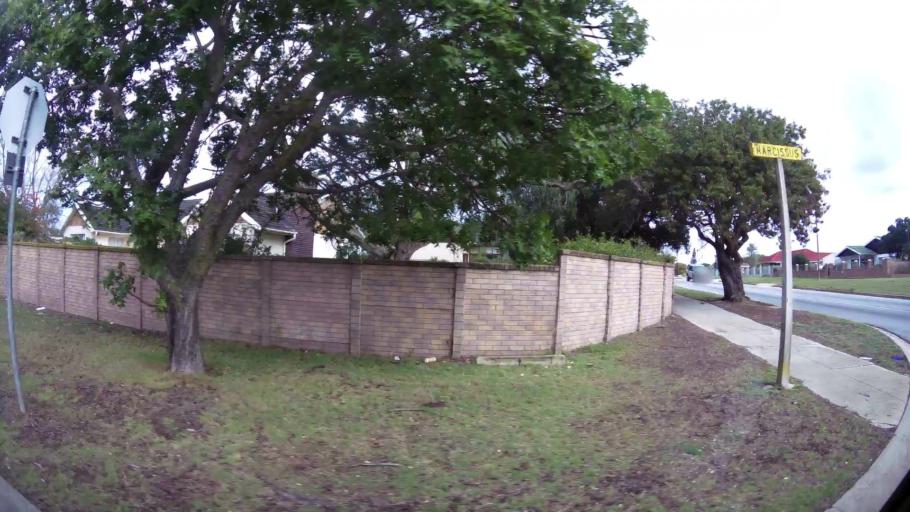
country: ZA
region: Eastern Cape
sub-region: Nelson Mandela Bay Metropolitan Municipality
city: Port Elizabeth
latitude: -33.9342
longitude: 25.5129
